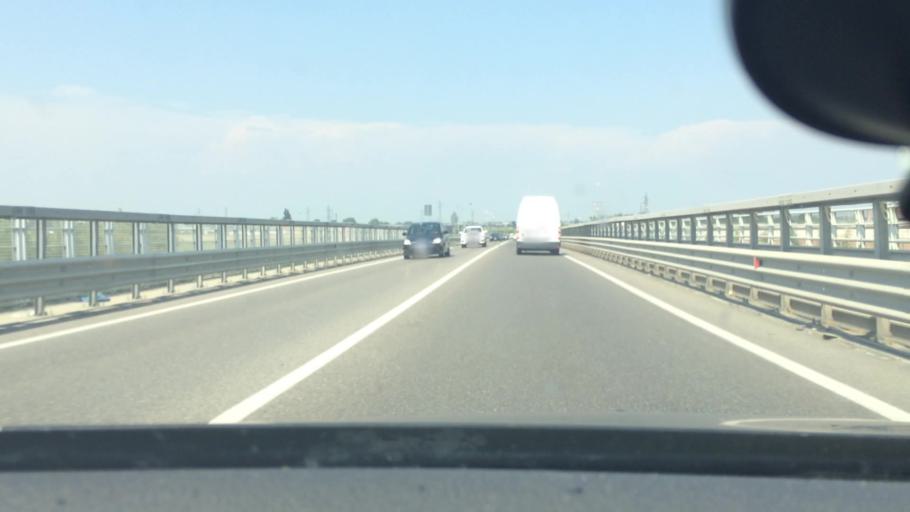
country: IT
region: Lombardy
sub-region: Provincia di Lodi
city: San Rocco al Porto
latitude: 45.0652
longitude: 9.7067
